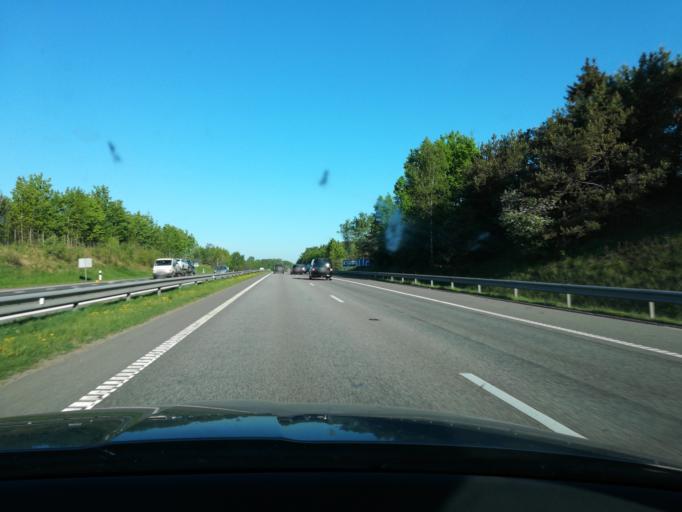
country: LT
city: Ziezmariai
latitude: 54.8019
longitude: 24.5143
